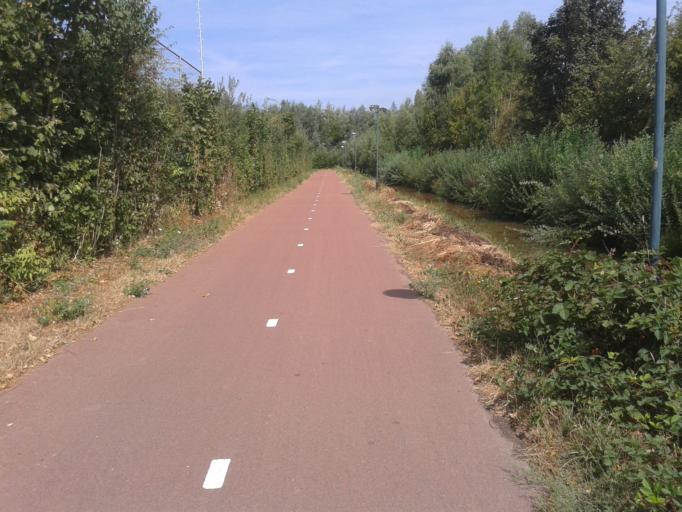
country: NL
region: North Brabant
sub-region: Gemeente Oisterwijk
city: Oisterwijk
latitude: 51.5714
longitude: 5.1780
